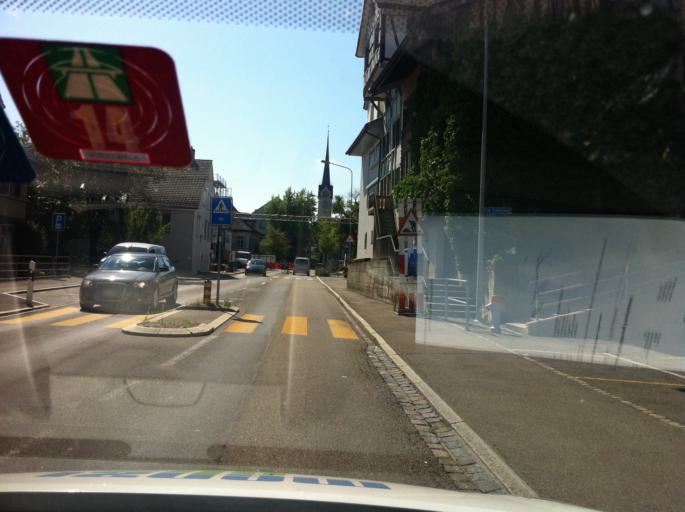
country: CH
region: Zurich
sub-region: Bezirk Horgen
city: Oberrieden / Berg
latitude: 47.2789
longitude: 8.5751
